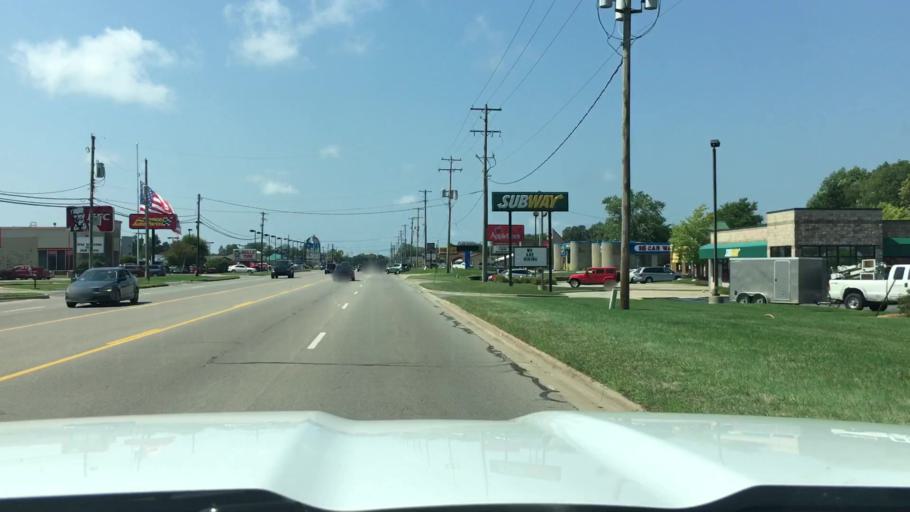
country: US
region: Michigan
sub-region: Allegan County
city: Plainwell
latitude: 42.4500
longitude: -85.6644
